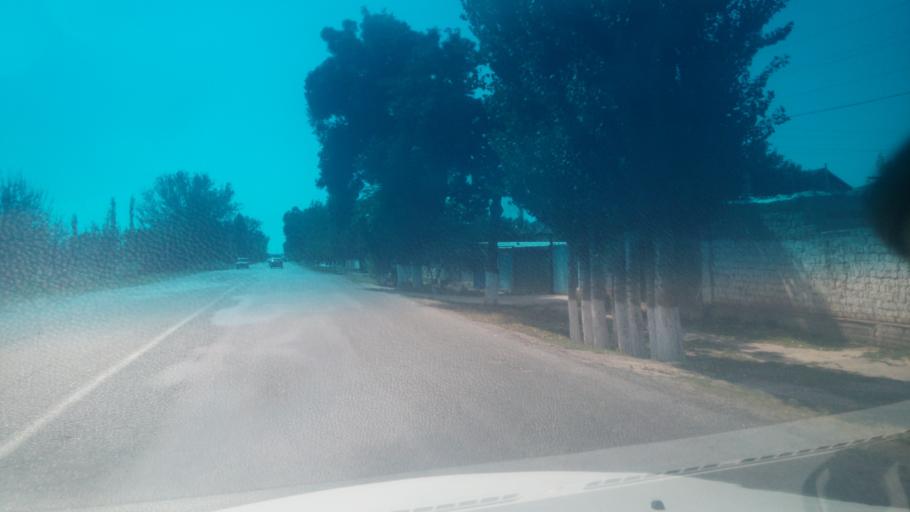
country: UZ
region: Sirdaryo
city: Sirdaryo
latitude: 40.8136
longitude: 68.6751
